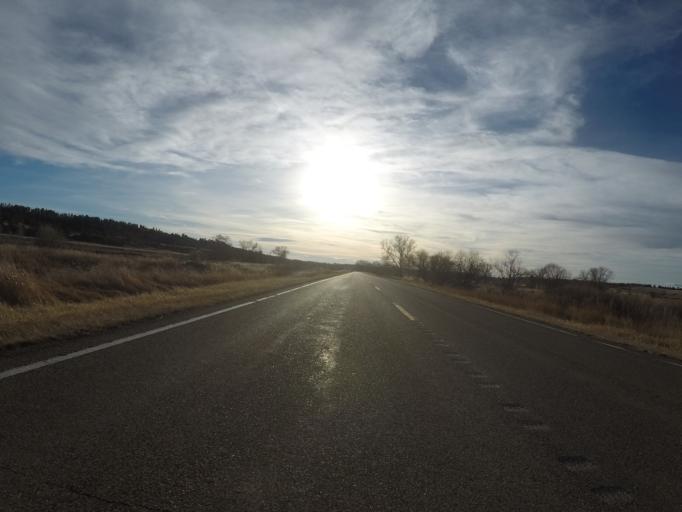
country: US
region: Montana
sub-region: Musselshell County
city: Roundup
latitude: 46.3467
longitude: -108.6800
